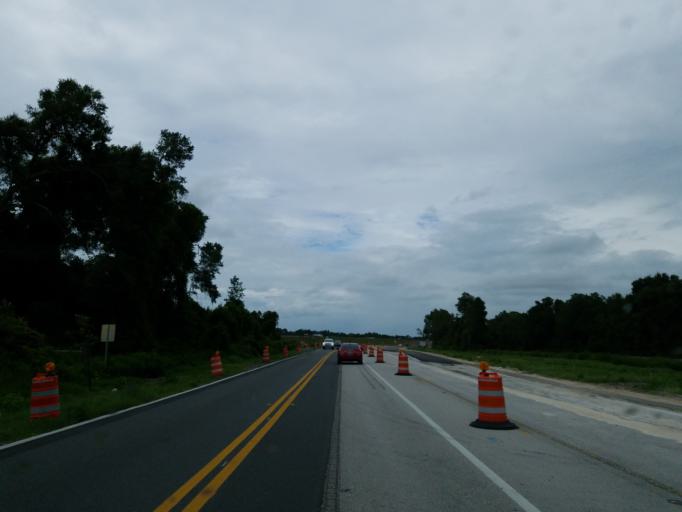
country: US
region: Florida
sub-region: Sumter County
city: Lake Panasoffkee
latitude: 28.7485
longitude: -82.1035
